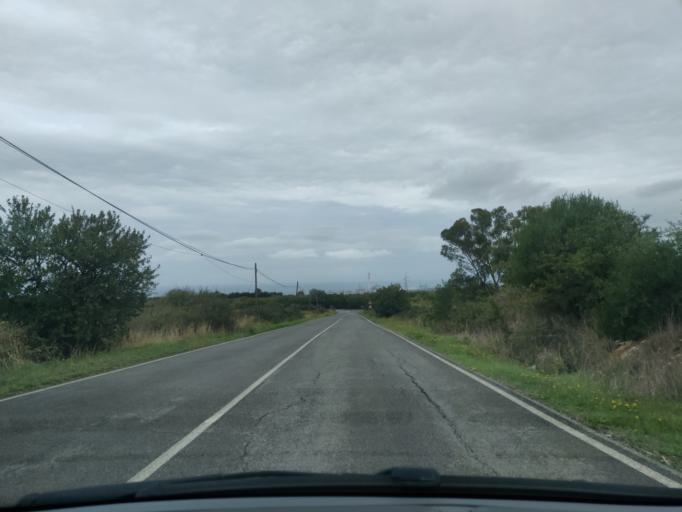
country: IT
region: Latium
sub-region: Citta metropolitana di Roma Capitale
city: Civitavecchia
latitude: 42.1073
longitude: 11.8363
